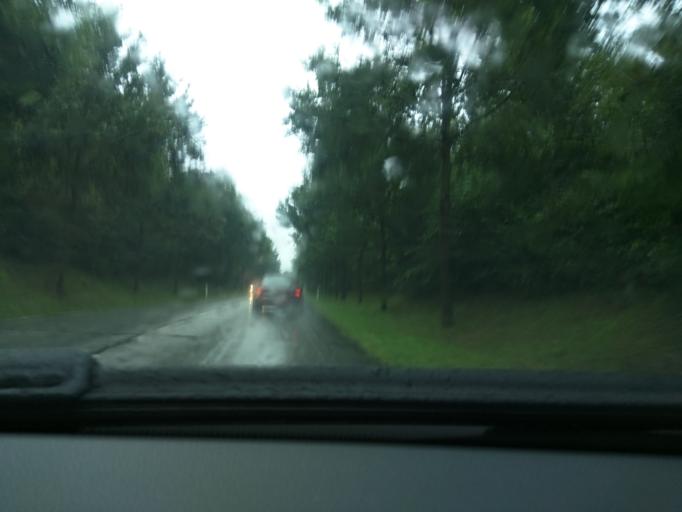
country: DE
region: Schleswig-Holstein
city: Schwarzenbek
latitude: 53.5091
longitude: 10.4747
